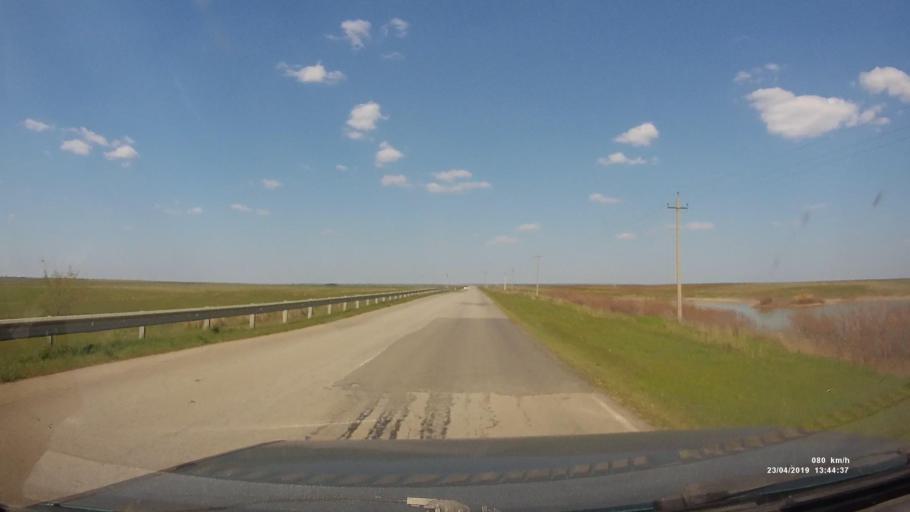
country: RU
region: Kalmykiya
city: Yashalta
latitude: 46.5831
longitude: 42.8172
